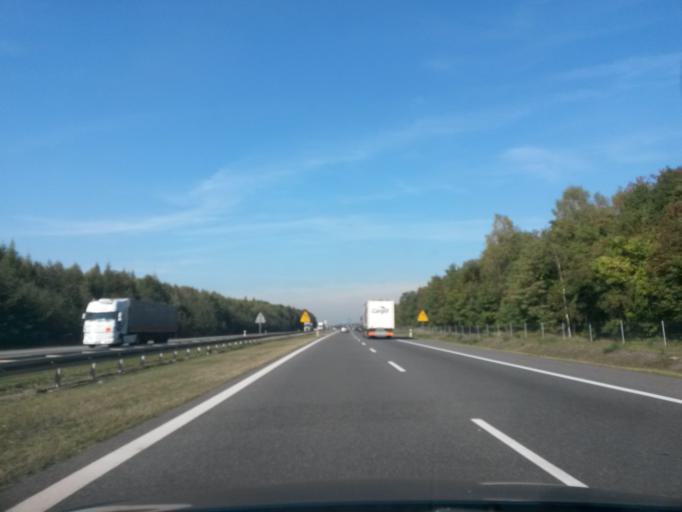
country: PL
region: Silesian Voivodeship
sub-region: Myslowice
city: Myslowice
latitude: 50.1889
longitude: 19.1902
